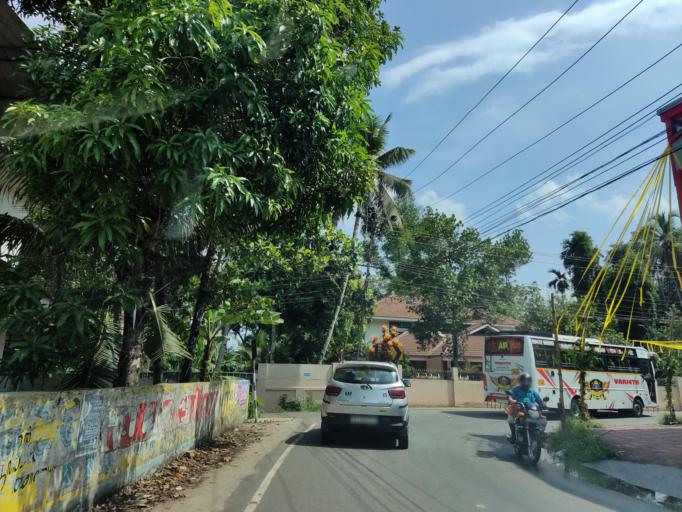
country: IN
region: Kerala
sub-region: Alappuzha
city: Mavelikara
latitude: 9.3226
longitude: 76.5157
